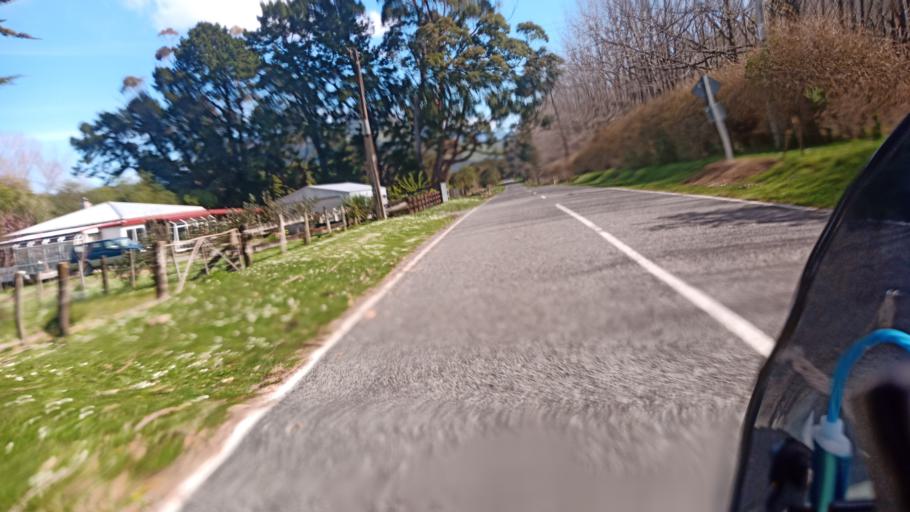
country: NZ
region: Gisborne
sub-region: Gisborne District
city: Gisborne
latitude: -37.8626
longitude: 178.2440
